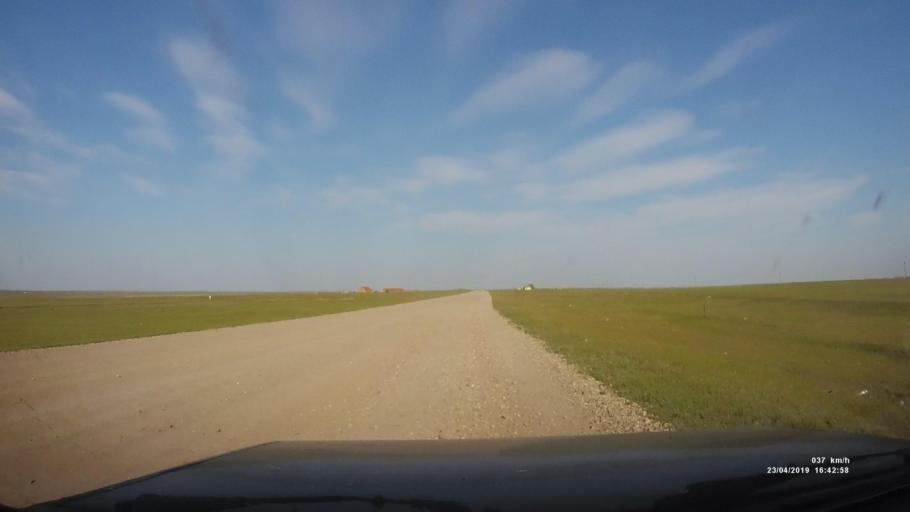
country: RU
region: Kalmykiya
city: Priyutnoye
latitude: 46.3478
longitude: 43.1976
